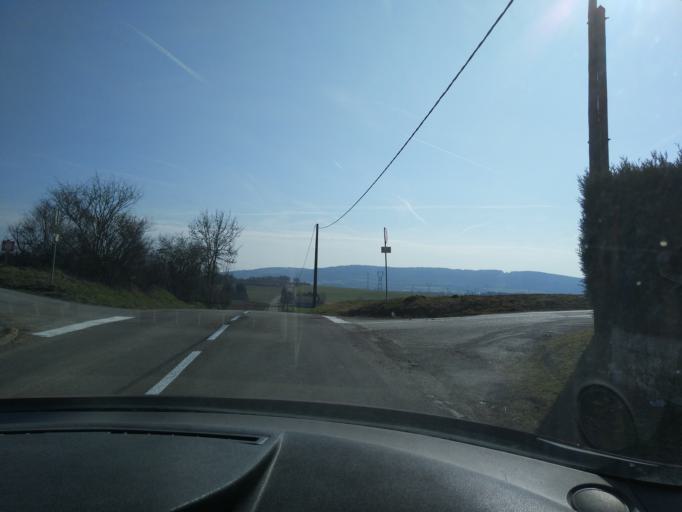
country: FR
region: Franche-Comte
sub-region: Departement du Doubs
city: Saone
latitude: 47.2194
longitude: 6.1260
